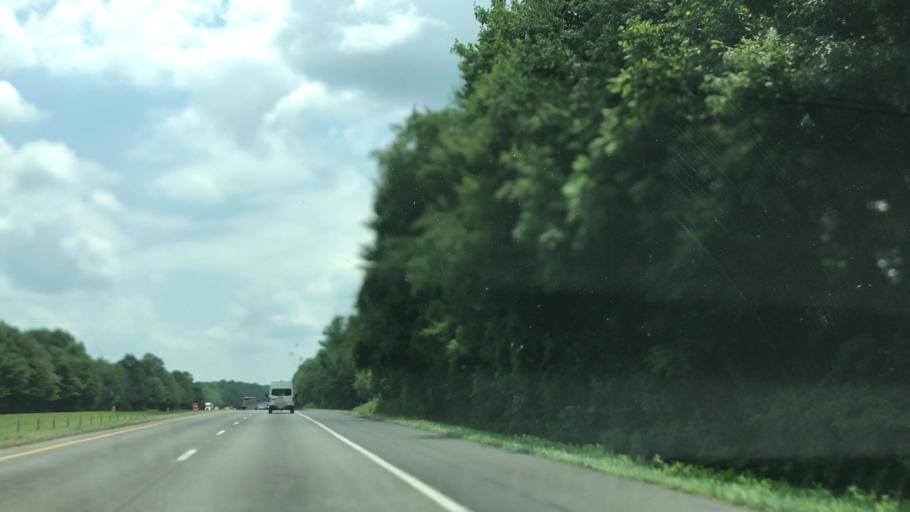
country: US
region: North Carolina
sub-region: Surry County
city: Dobson
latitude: 36.4212
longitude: -80.7777
